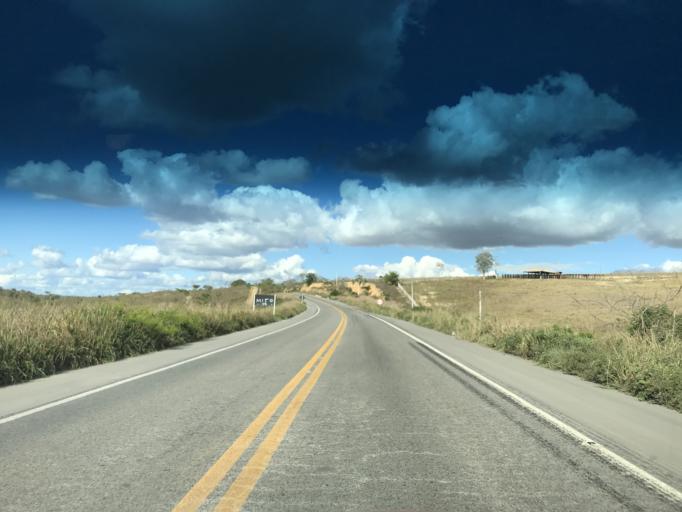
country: BR
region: Bahia
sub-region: Andarai
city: Vera Cruz
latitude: -12.4614
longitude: -40.8948
